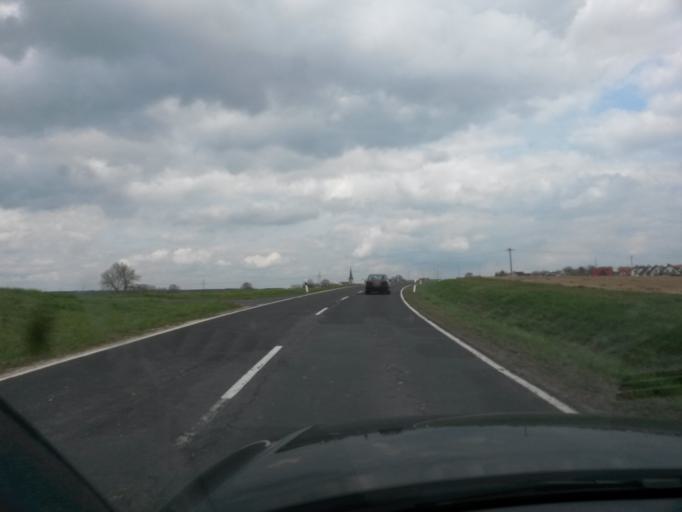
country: DE
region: Bavaria
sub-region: Regierungsbezirk Unterfranken
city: Oberpleichfeld
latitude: 49.8747
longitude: 10.0760
